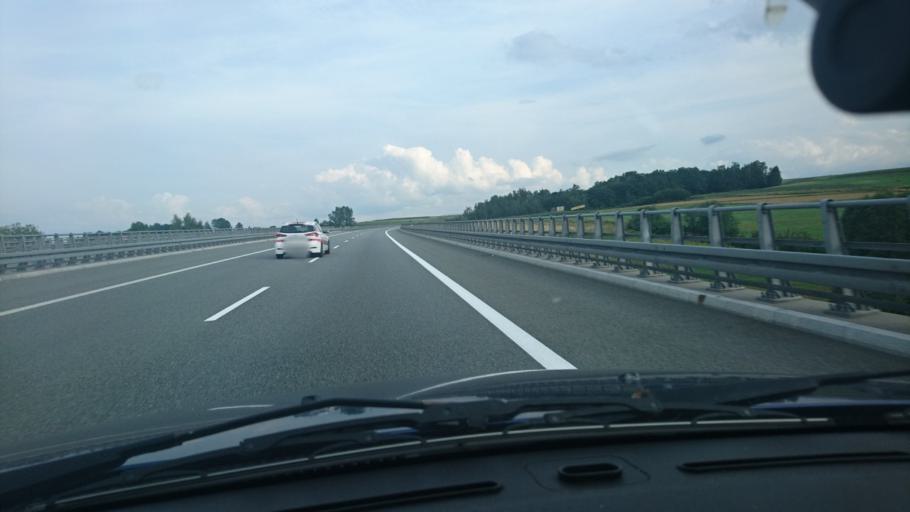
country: PL
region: Silesian Voivodeship
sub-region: Powiat zywiecki
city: Lesna
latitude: 49.6985
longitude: 19.1312
